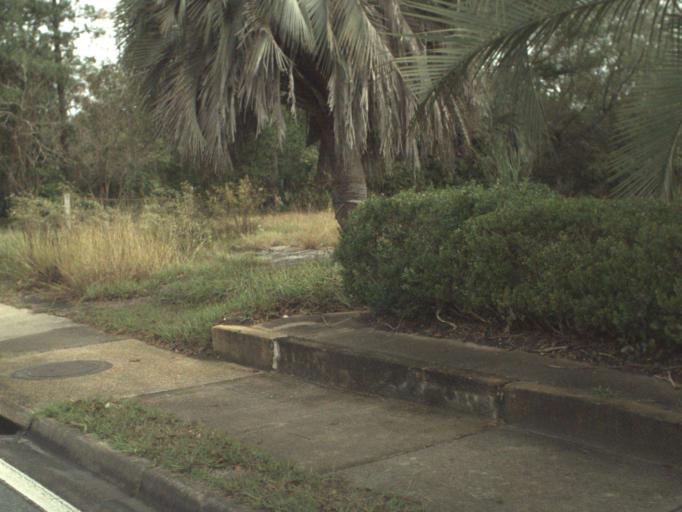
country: US
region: Florida
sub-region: Gadsden County
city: Havana
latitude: 30.6270
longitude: -84.4152
